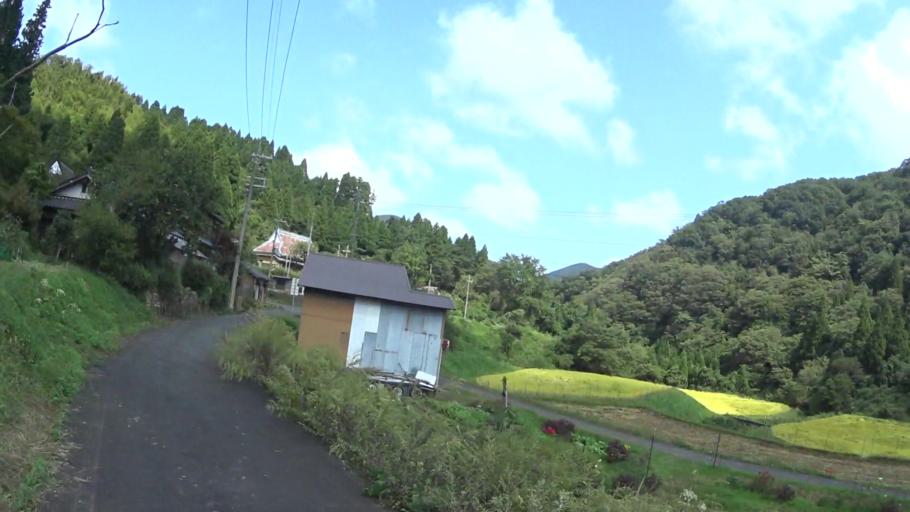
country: JP
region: Kyoto
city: Miyazu
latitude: 35.7188
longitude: 135.2096
